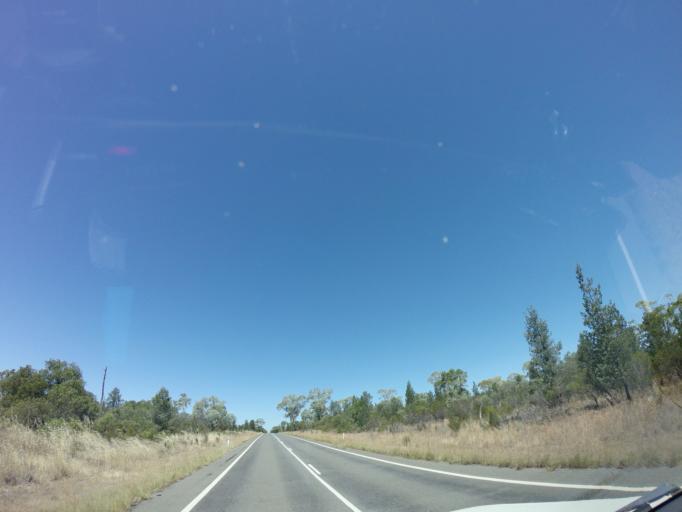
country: AU
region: New South Wales
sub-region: Bogan
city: Nyngan
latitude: -31.5508
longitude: 146.6747
